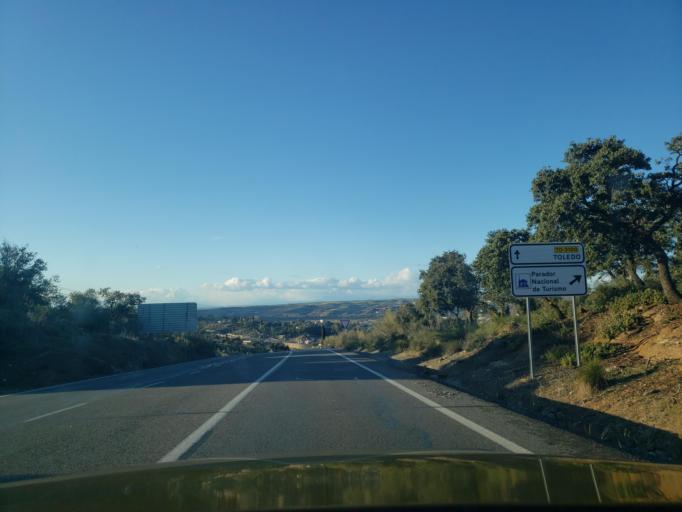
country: ES
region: Castille-La Mancha
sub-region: Province of Toledo
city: Toledo
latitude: 39.8462
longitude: -4.0239
